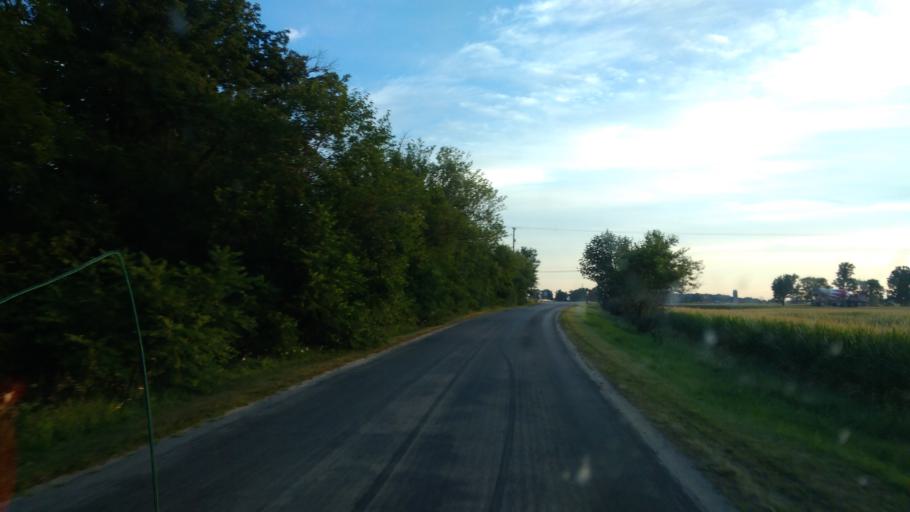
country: US
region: Indiana
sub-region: Adams County
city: Berne
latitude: 40.6546
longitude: -85.0322
